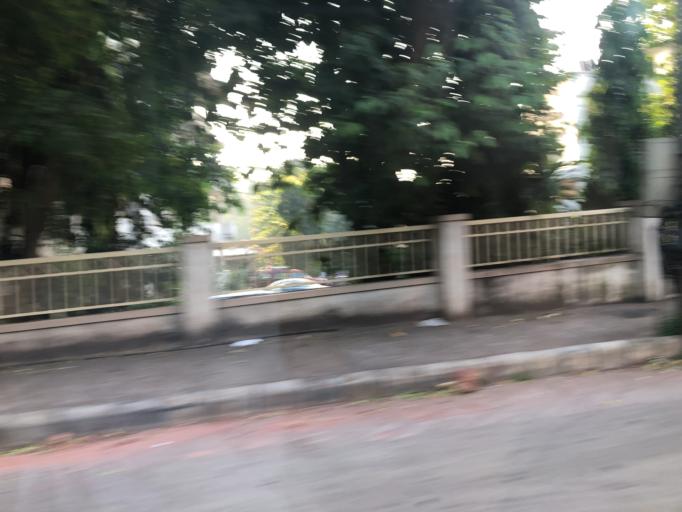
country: IN
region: Karnataka
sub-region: Dakshina Kannada
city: Mangalore
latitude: 12.8743
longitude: 74.8487
